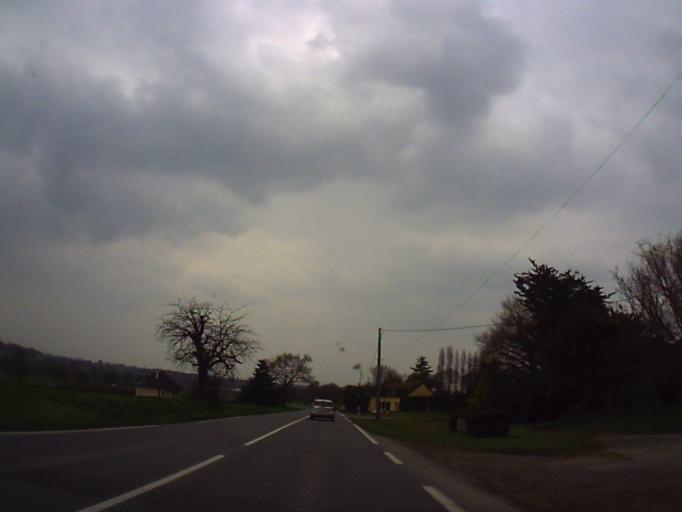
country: FR
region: Brittany
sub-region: Departement d'Ille-et-Vilaine
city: Vezin-le-Coquet
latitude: 48.1226
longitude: -1.7787
